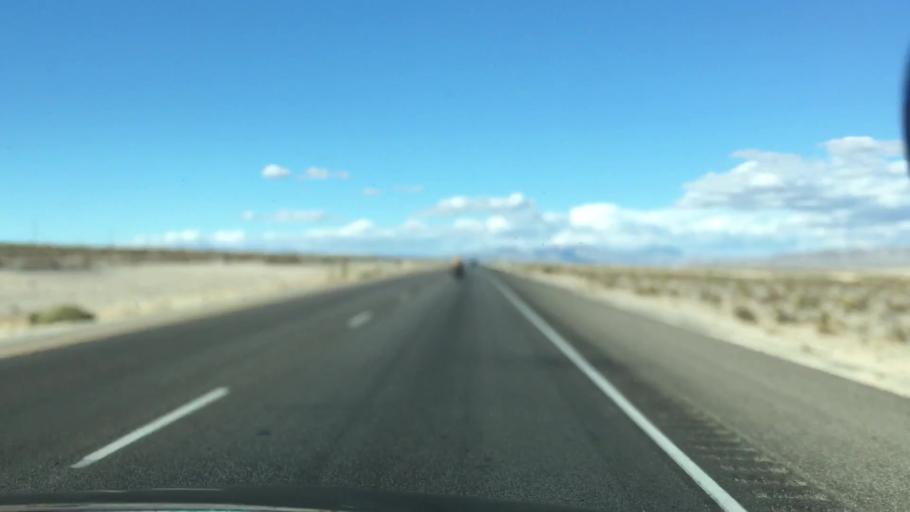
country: US
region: Nevada
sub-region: Clark County
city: Summerlin South
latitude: 36.4355
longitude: -115.4294
